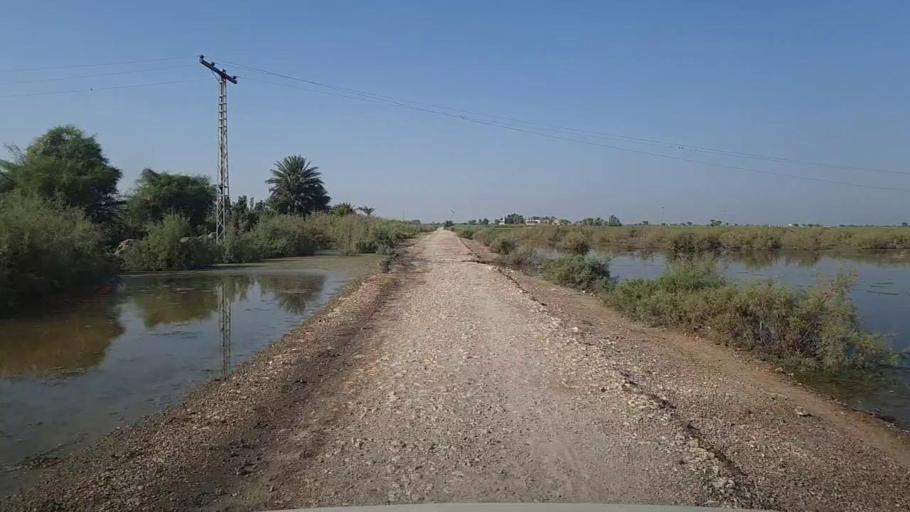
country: PK
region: Sindh
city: Kandhkot
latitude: 28.3801
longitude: 69.3563
